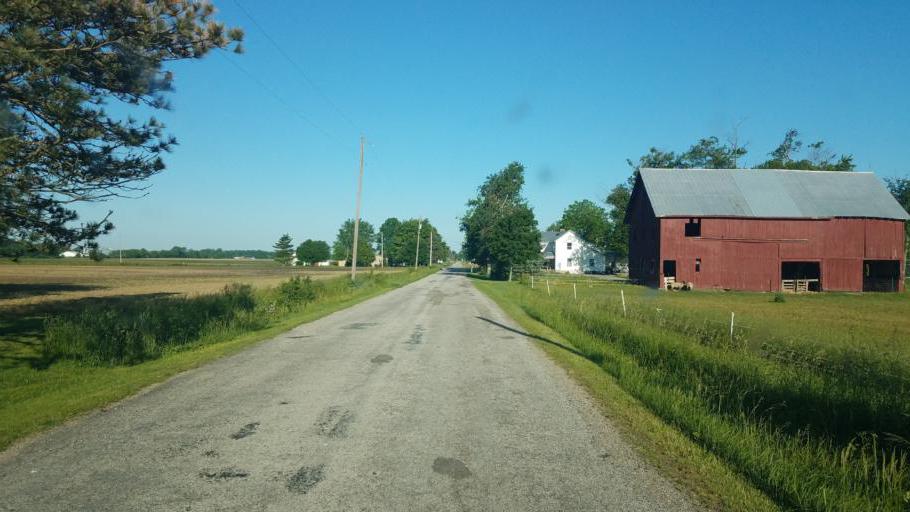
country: US
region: Ohio
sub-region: Morrow County
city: Mount Gilead
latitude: 40.6161
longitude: -82.9159
